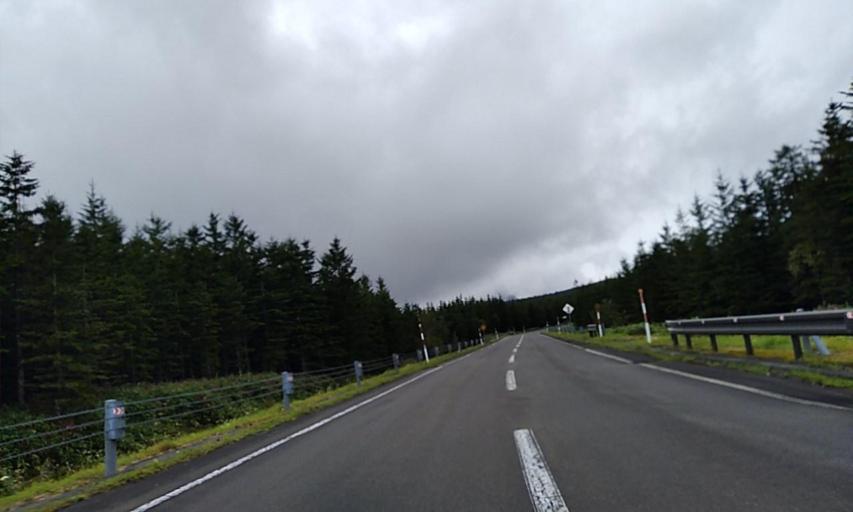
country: JP
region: Hokkaido
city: Abashiri
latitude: 43.6092
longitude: 144.5923
